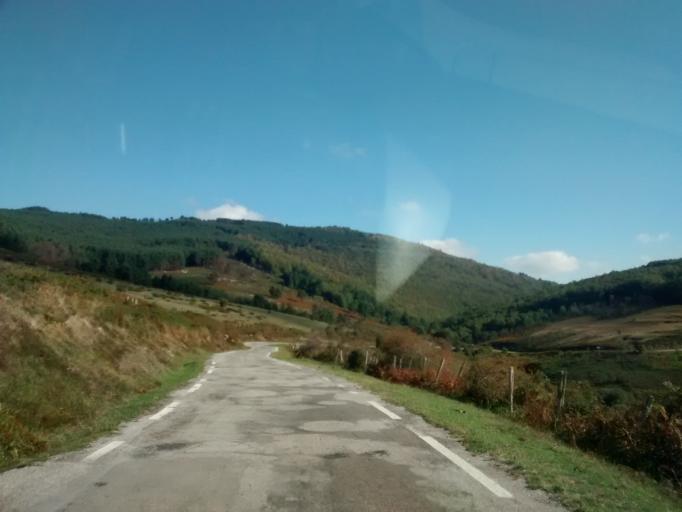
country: ES
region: Castille and Leon
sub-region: Provincia de Burgos
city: Arija
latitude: 42.9300
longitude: -4.0192
